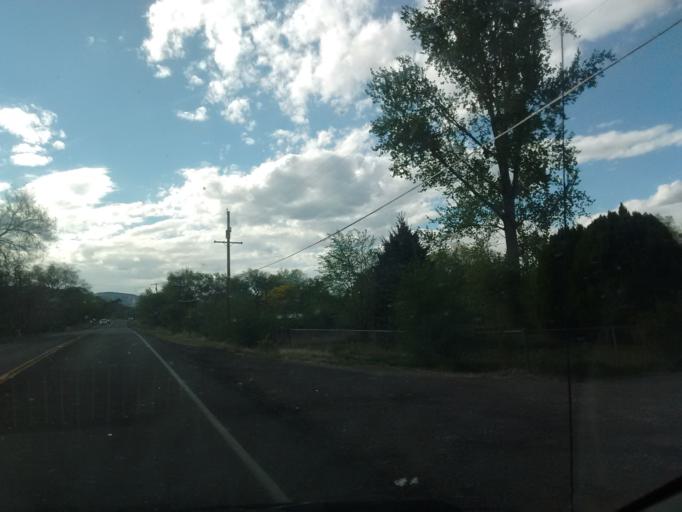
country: US
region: Colorado
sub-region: Mesa County
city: Redlands
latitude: 39.0752
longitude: -108.6274
